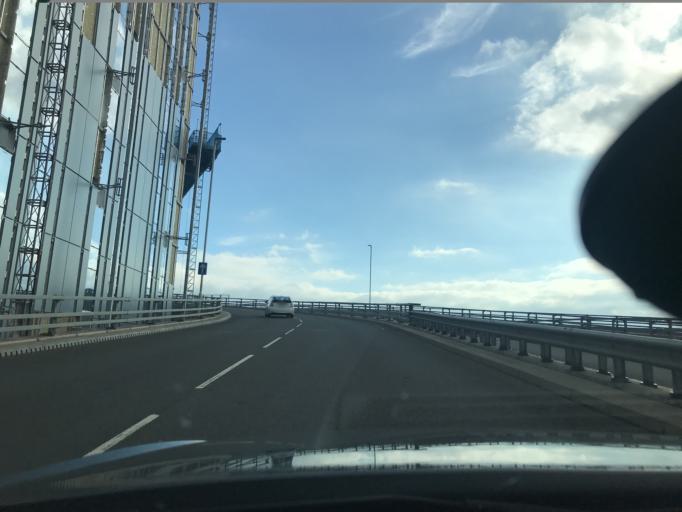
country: GB
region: England
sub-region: Greater London
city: West Drayton
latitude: 51.4701
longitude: -0.4540
